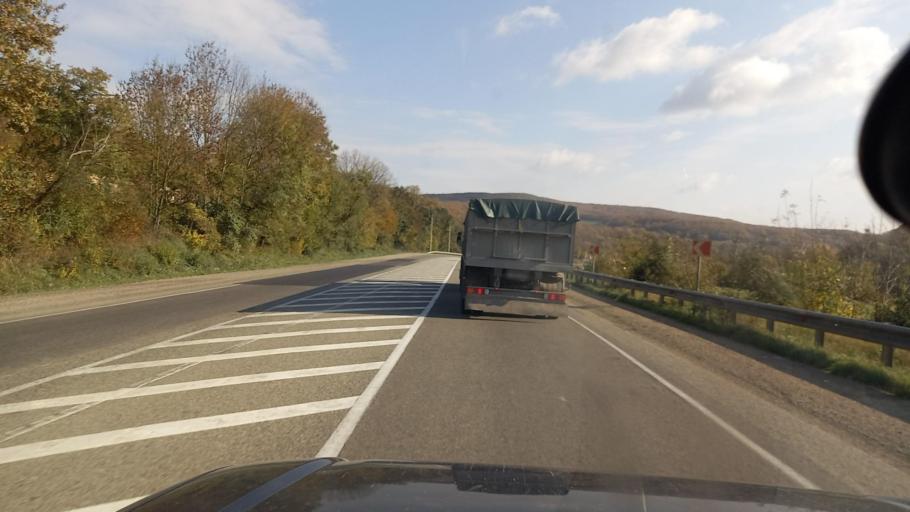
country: RU
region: Krasnodarskiy
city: Gayduk
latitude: 44.8749
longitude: 37.7744
